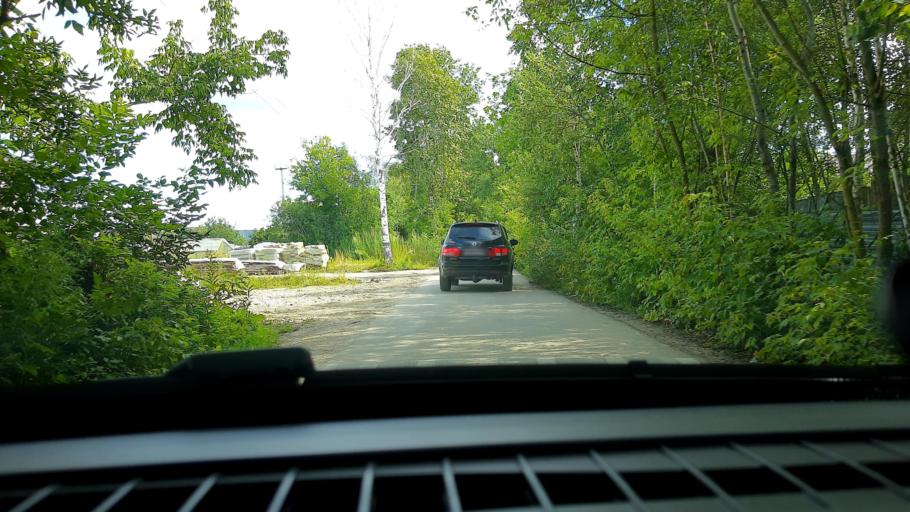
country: RU
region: Nizjnij Novgorod
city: Gorbatovka
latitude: 56.2495
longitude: 43.8138
